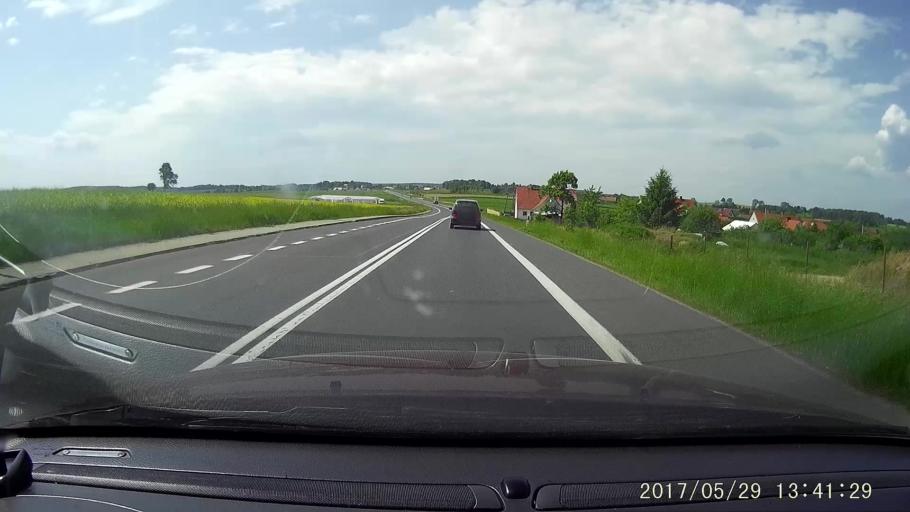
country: PL
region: Lower Silesian Voivodeship
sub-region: Powiat lubanski
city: Pisarzowice
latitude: 51.1339
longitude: 15.2548
